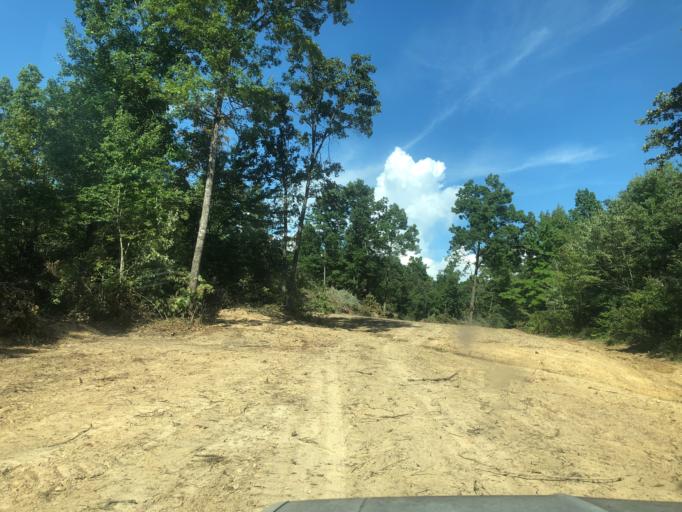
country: US
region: Tennessee
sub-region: Fentress County
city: Jamestown
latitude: 36.3190
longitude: -84.8530
